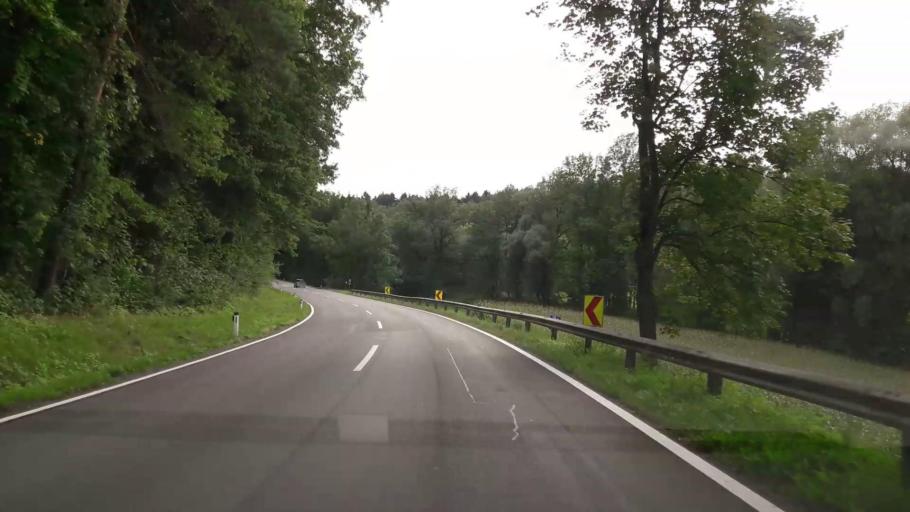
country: AT
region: Styria
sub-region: Politischer Bezirk Hartberg-Fuerstenfeld
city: Hartberg
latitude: 47.2647
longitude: 15.9390
